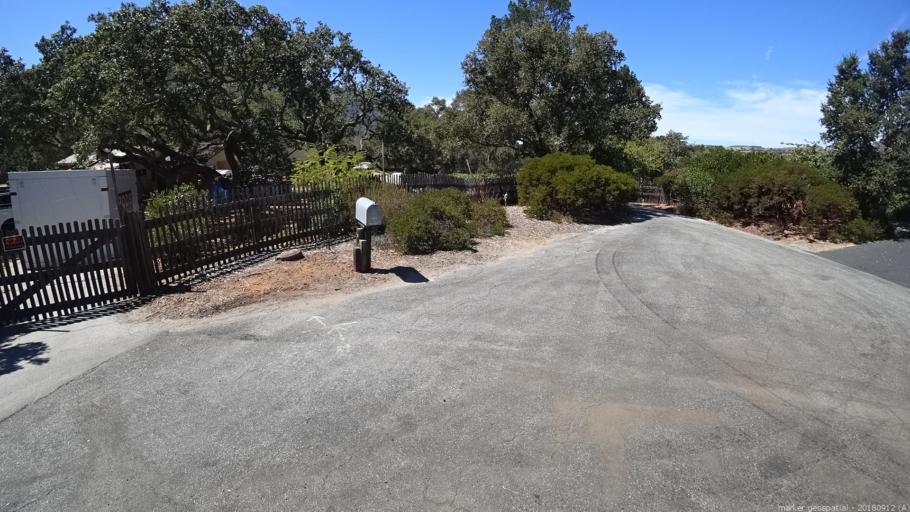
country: US
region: California
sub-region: Monterey County
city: Carmel Valley Village
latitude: 36.4998
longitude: -121.7489
